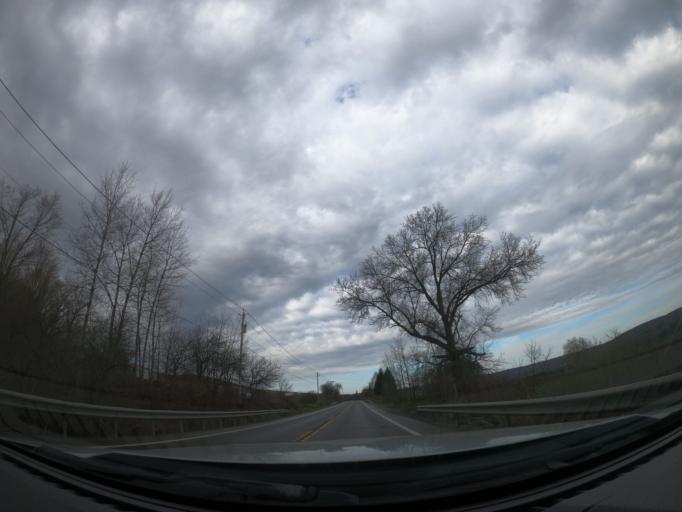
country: US
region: New York
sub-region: Madison County
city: Cazenovia
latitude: 42.7515
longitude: -75.9158
